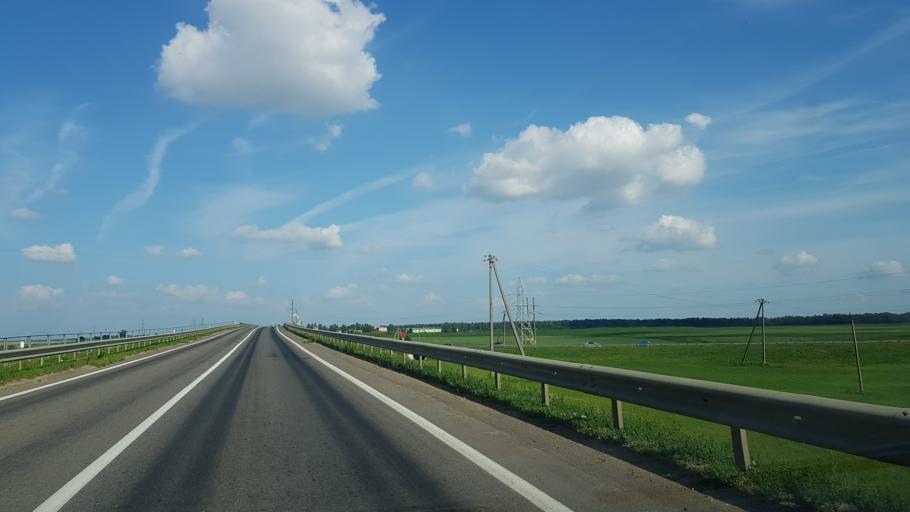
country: BY
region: Minsk
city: Stan'kava
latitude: 53.7043
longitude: 27.2122
